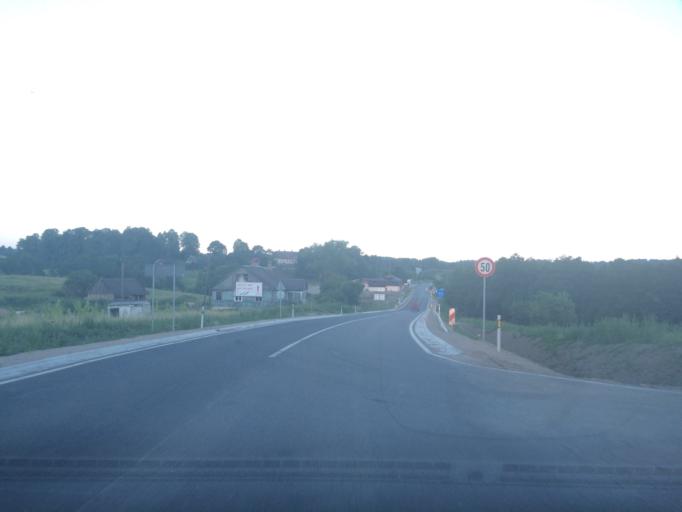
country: LT
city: Zarasai
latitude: 55.7461
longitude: 26.3125
